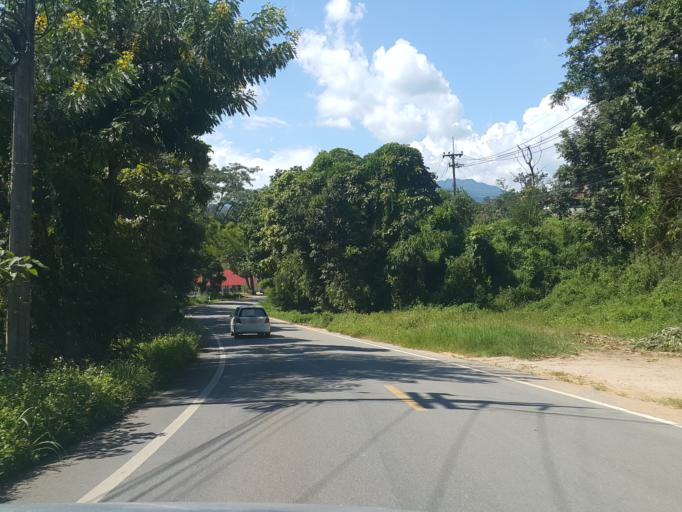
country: TH
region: Chiang Mai
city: Mae Taeng
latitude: 19.1904
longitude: 98.8996
